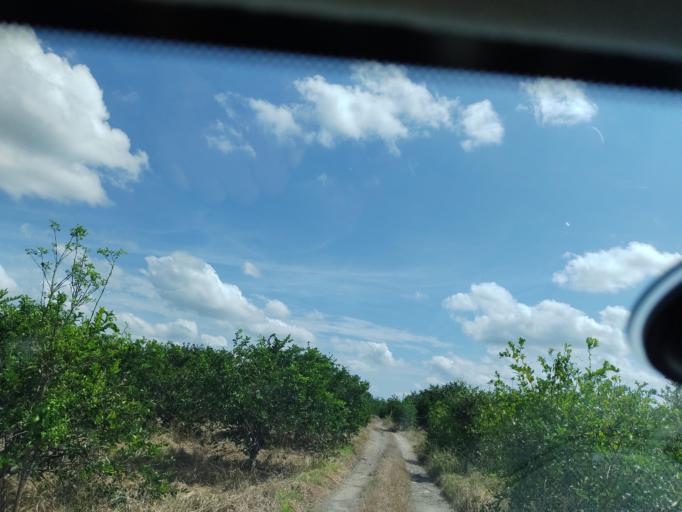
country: MX
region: Veracruz
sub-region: Martinez de la Torre
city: El Progreso
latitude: 20.1136
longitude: -97.0060
